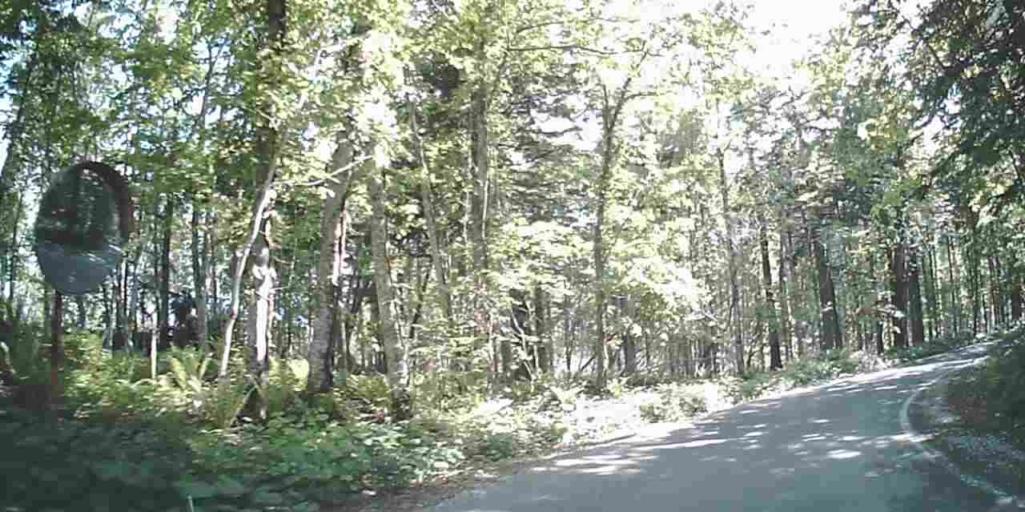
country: JP
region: Hokkaido
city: Shiraoi
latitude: 42.7239
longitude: 141.4136
